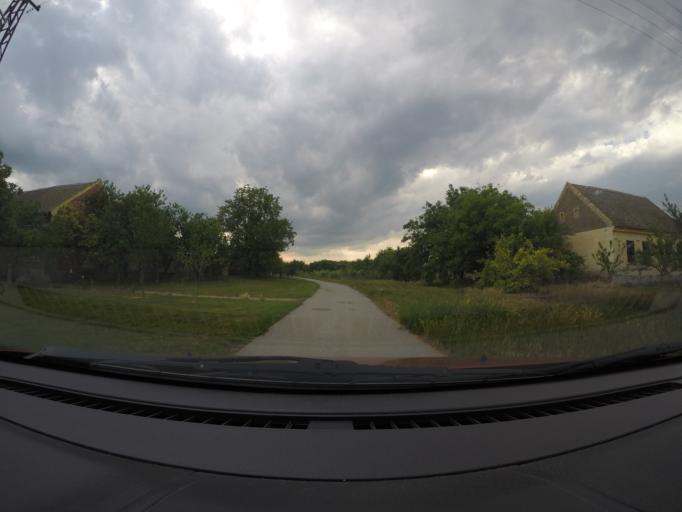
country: RS
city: Uzdin
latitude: 45.2054
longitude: 20.6144
